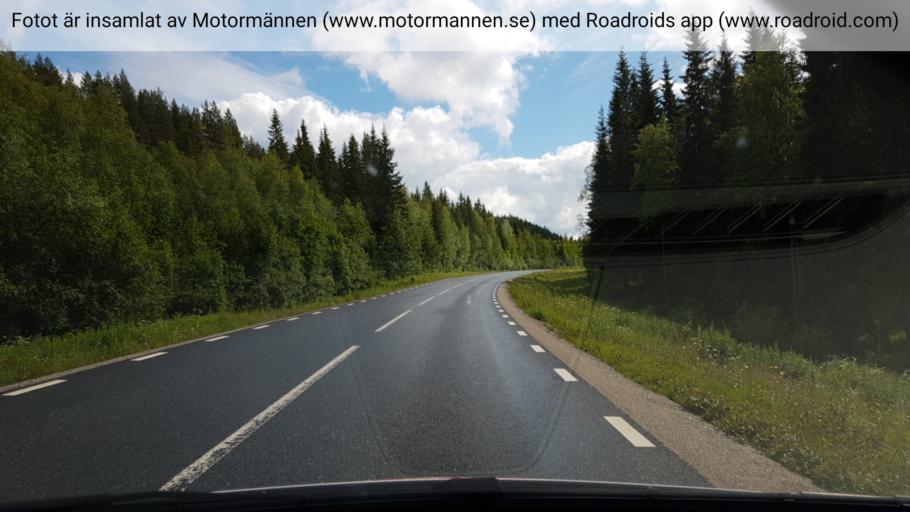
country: SE
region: Vaesterbotten
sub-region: Bjurholms Kommun
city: Bjurholm
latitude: 64.3766
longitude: 19.1394
